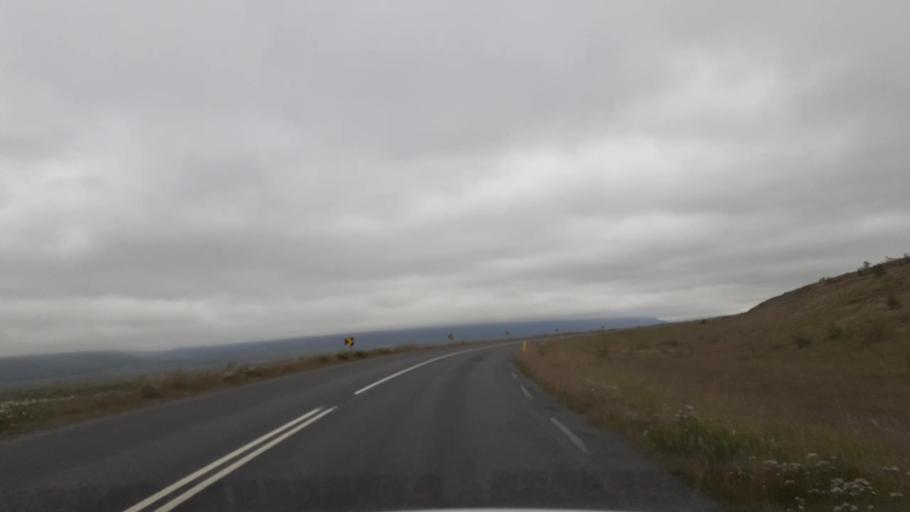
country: IS
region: Northwest
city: Saudarkrokur
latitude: 65.5650
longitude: -19.4620
